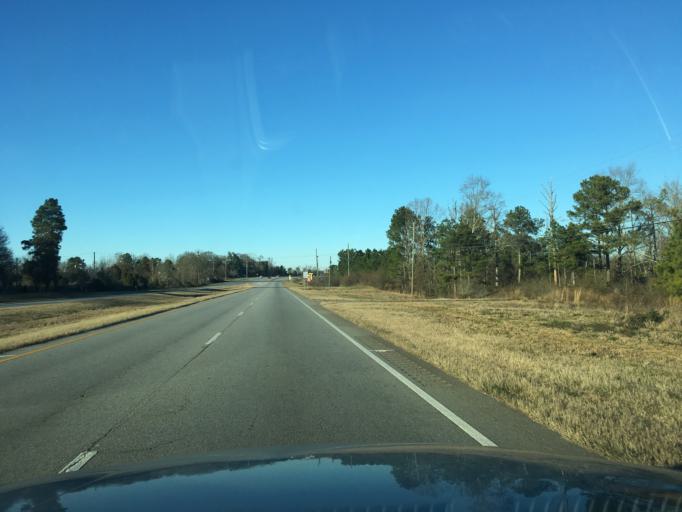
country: US
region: Georgia
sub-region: Carroll County
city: Carrollton
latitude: 33.5077
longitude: -85.0792
